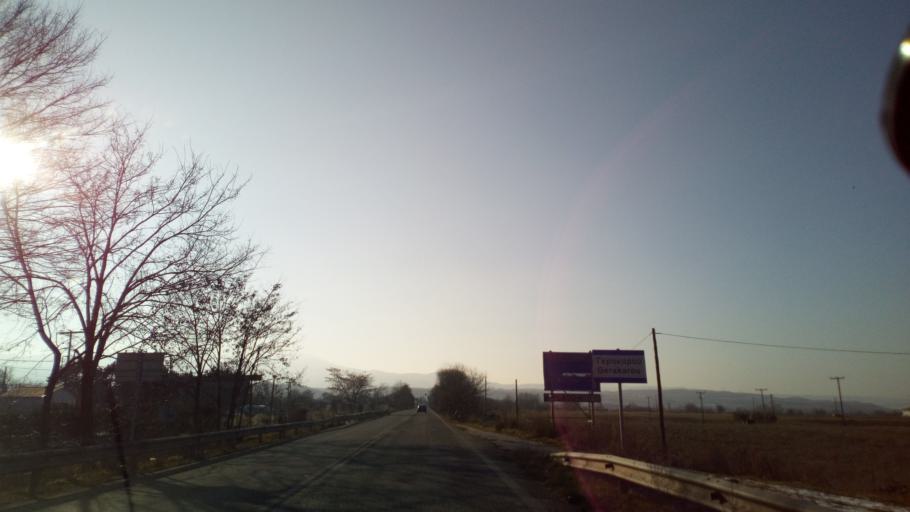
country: GR
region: Central Macedonia
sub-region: Nomos Thessalonikis
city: Gerakarou
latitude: 40.6319
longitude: 23.2227
